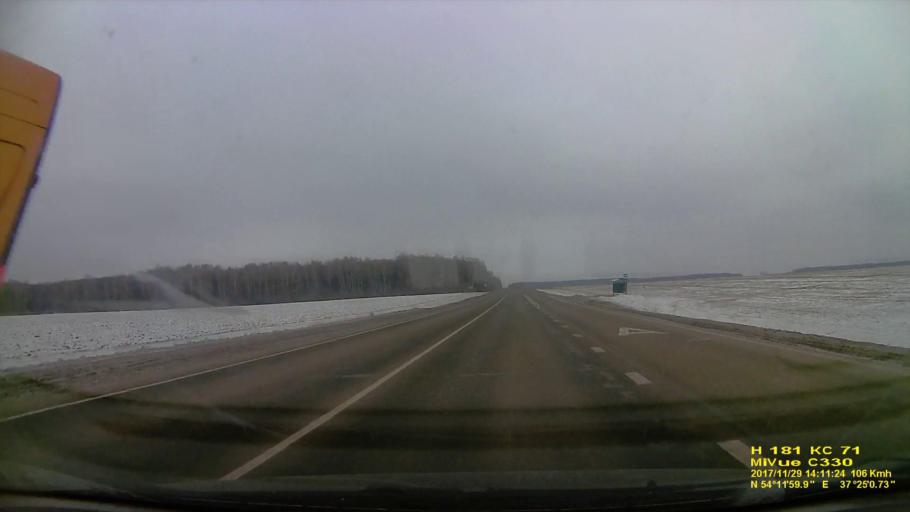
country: RU
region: Tula
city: Barsuki
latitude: 54.1998
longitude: 37.4171
